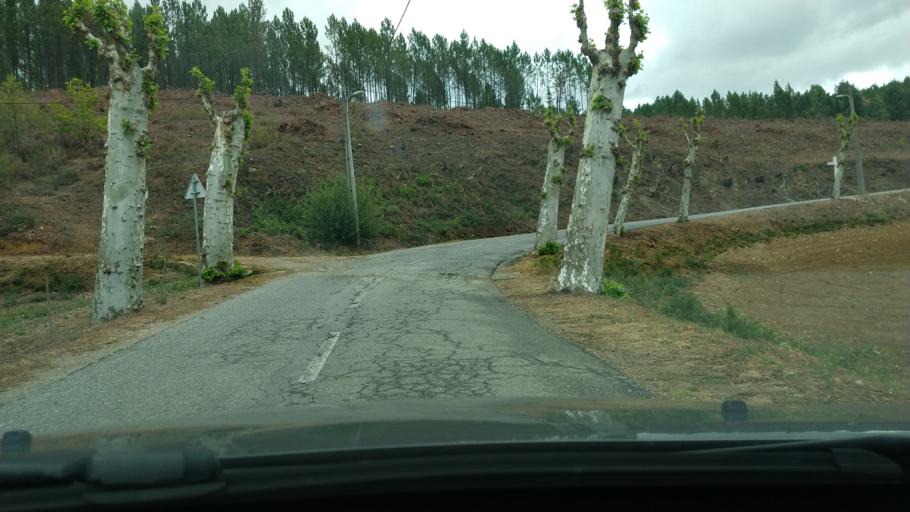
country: PT
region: Castelo Branco
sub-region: Covilha
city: Covilha
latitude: 40.2253
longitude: -7.6419
